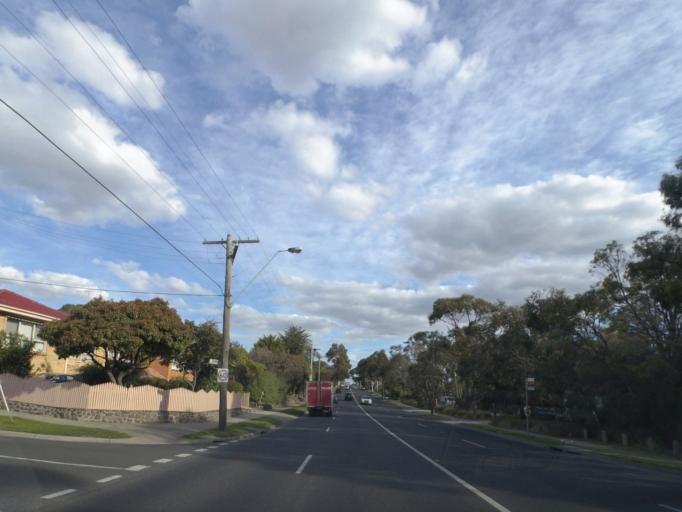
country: AU
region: Victoria
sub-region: Whitehorse
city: Burwood
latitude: -37.8600
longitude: 145.1320
